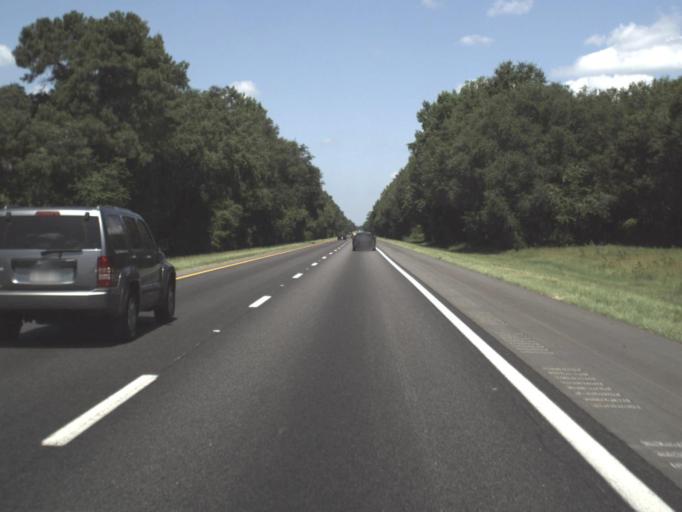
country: US
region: Florida
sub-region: Madison County
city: Madison
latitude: 30.4057
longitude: -83.3993
